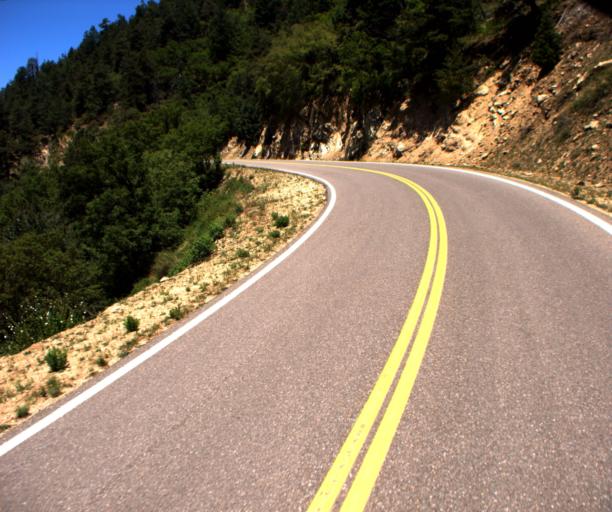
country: US
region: Arizona
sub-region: Graham County
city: Swift Trail Junction
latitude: 32.6276
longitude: -109.8359
